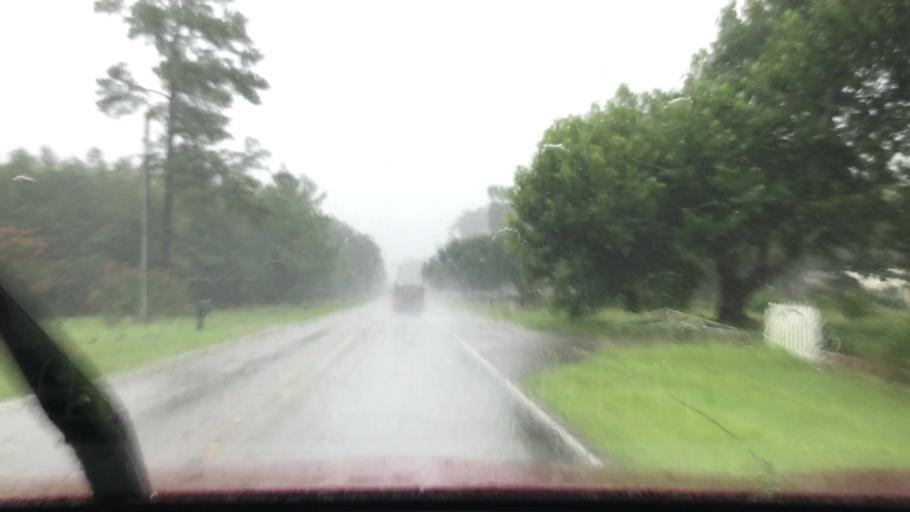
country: US
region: South Carolina
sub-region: Horry County
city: Red Hill
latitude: 33.8984
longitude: -78.9290
